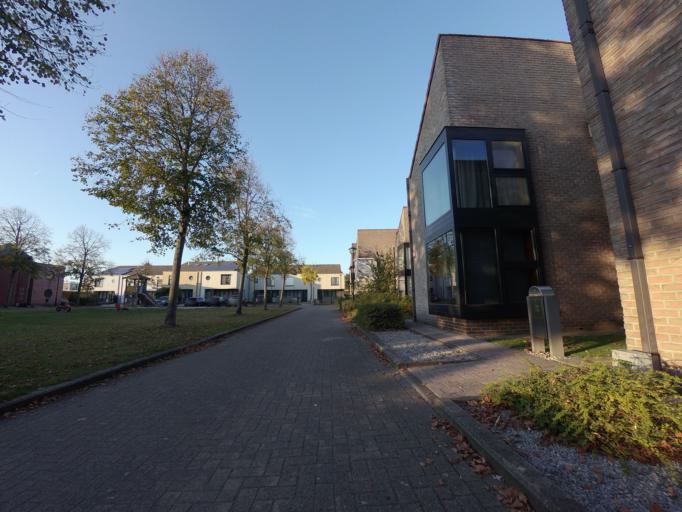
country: BE
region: Flanders
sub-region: Provincie Antwerpen
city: Stabroek
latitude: 51.3476
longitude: 4.3216
